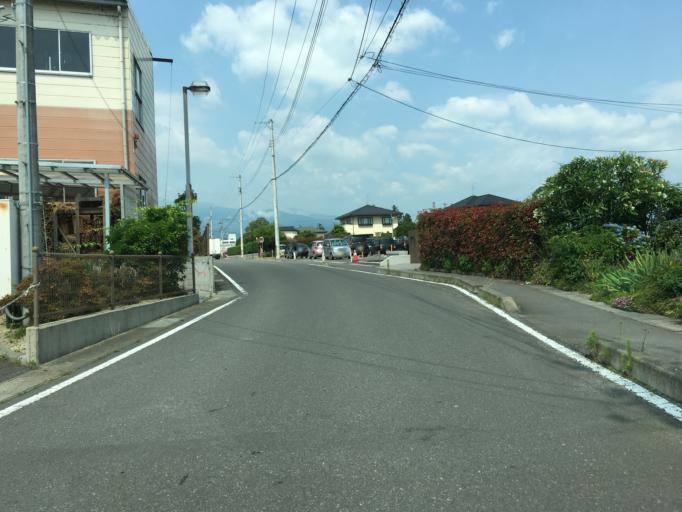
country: JP
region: Fukushima
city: Fukushima-shi
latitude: 37.7393
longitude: 140.4434
